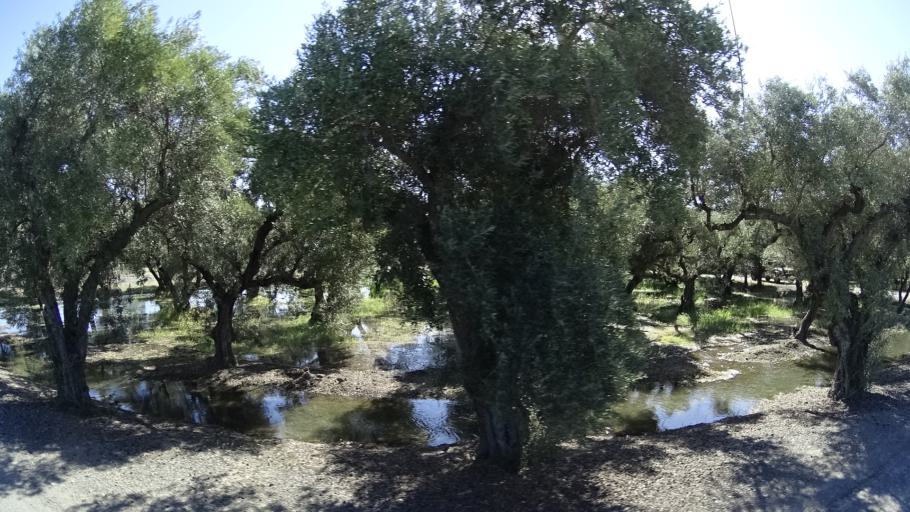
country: US
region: California
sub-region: Glenn County
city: Orland
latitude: 39.7357
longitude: -122.1688
